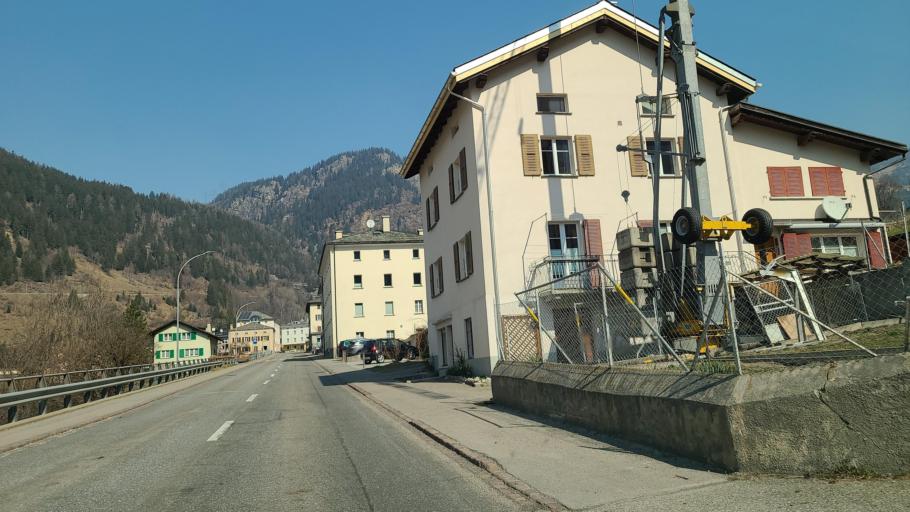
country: CH
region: Grisons
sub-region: Bernina District
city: Poschiavo
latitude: 46.3387
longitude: 10.0606
